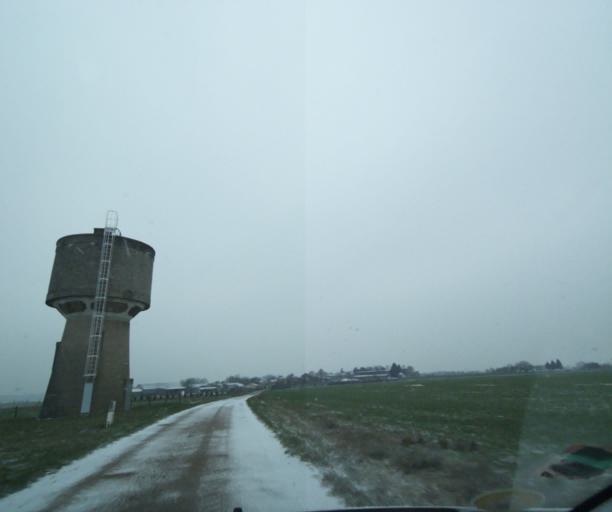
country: FR
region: Champagne-Ardenne
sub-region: Departement de la Haute-Marne
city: Wassy
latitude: 48.4680
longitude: 4.9985
